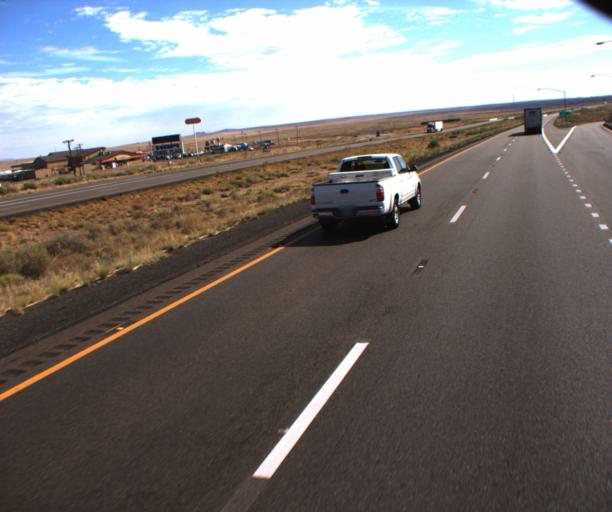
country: US
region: Arizona
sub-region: Navajo County
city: Holbrook
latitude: 34.9711
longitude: -110.0913
